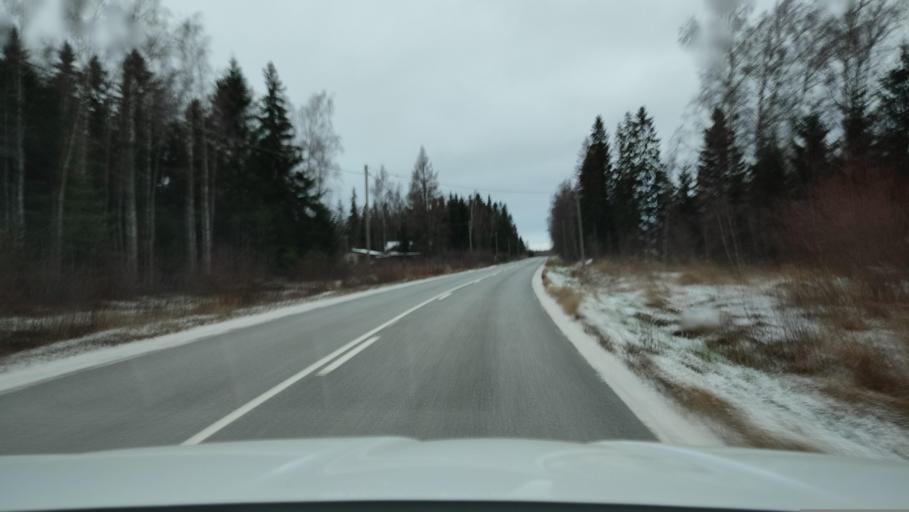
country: FI
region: Ostrobothnia
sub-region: Vaasa
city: Replot
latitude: 63.2673
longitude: 21.3483
